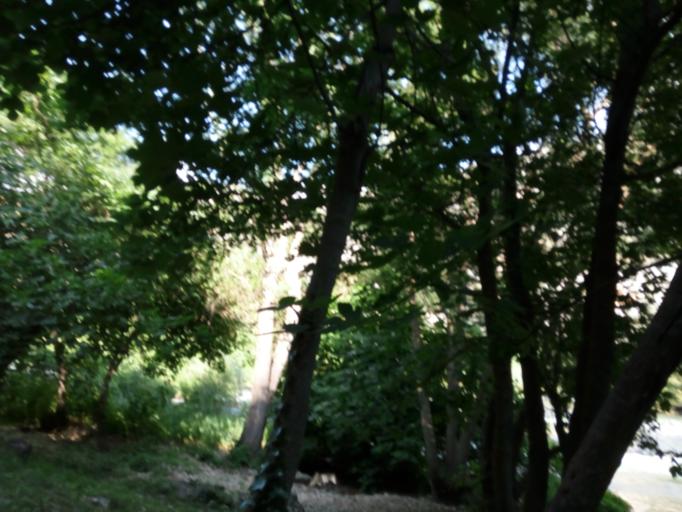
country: HR
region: Sibensko-Kniniska
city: Kistanje
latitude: 43.9070
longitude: 15.9759
